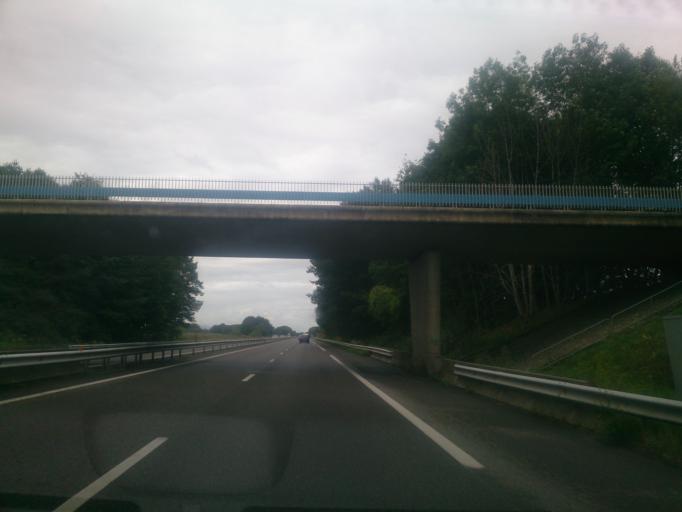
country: FR
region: Midi-Pyrenees
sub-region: Departement des Hautes-Pyrenees
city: Lannemezan
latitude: 43.1065
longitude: 0.4407
